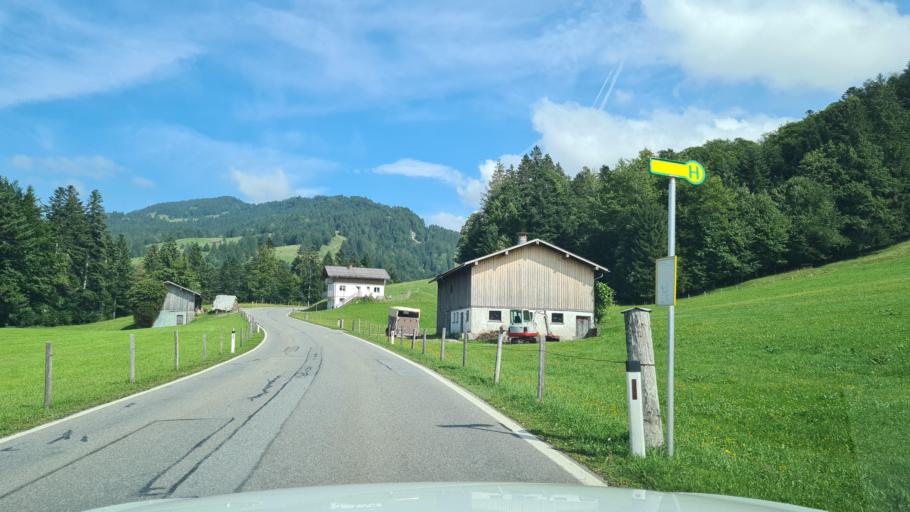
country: AT
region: Vorarlberg
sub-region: Politischer Bezirk Bregenz
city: Riefensberg
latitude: 47.4564
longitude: 9.9928
